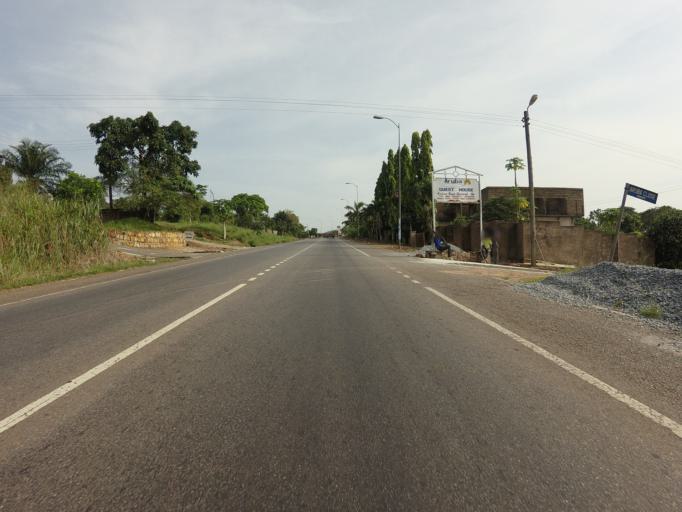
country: GH
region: Eastern
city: Aburi
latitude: 5.8257
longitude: -0.1856
